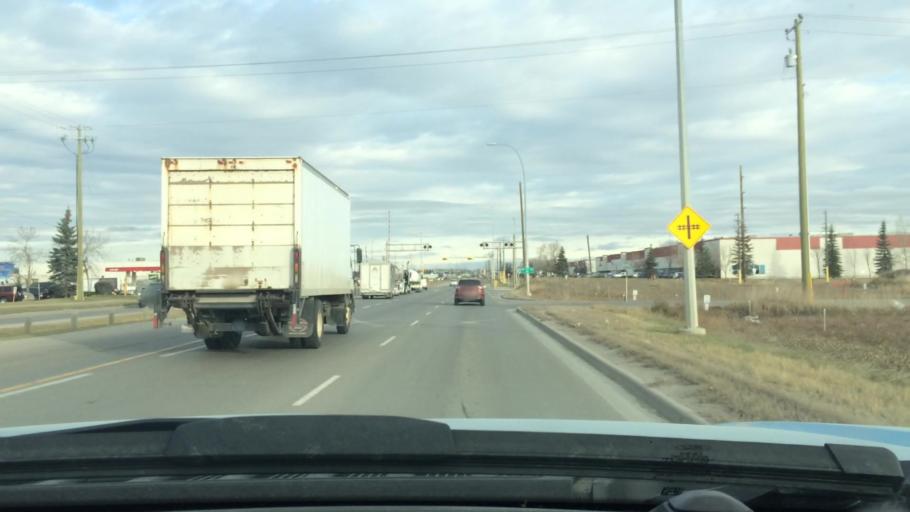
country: CA
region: Alberta
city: Calgary
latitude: 51.0073
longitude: -113.9583
